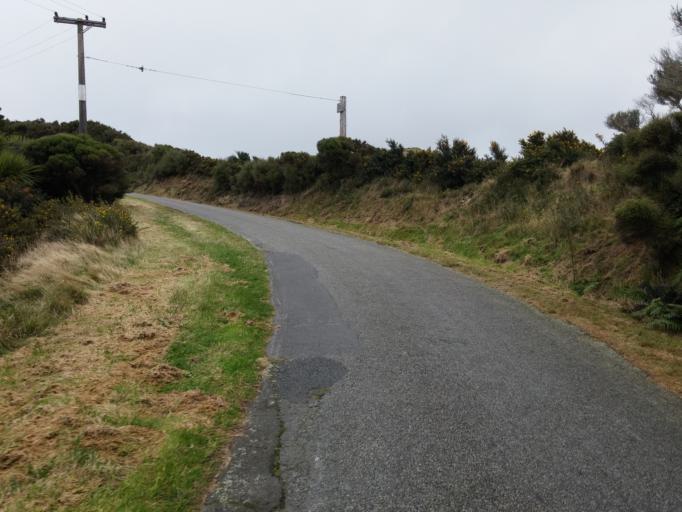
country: NZ
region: Wellington
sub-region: Wellington City
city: Brooklyn
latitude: -41.3214
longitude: 174.7317
